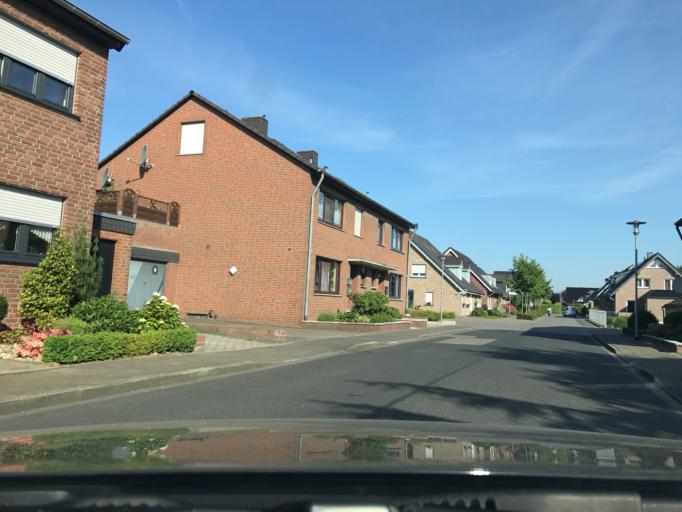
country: DE
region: North Rhine-Westphalia
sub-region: Regierungsbezirk Dusseldorf
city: Wachtendonk
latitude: 51.4035
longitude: 6.3541
